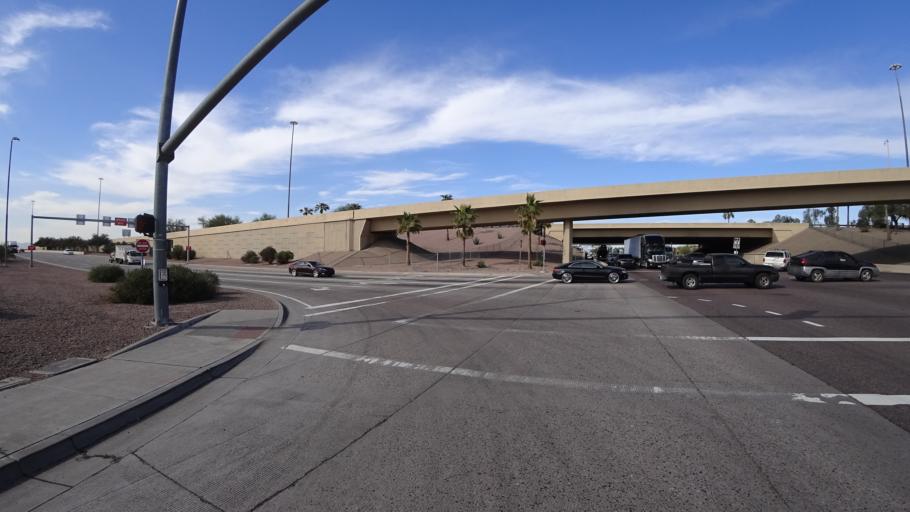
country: US
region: Arizona
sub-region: Maricopa County
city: Tolleson
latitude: 33.4606
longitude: -112.2727
